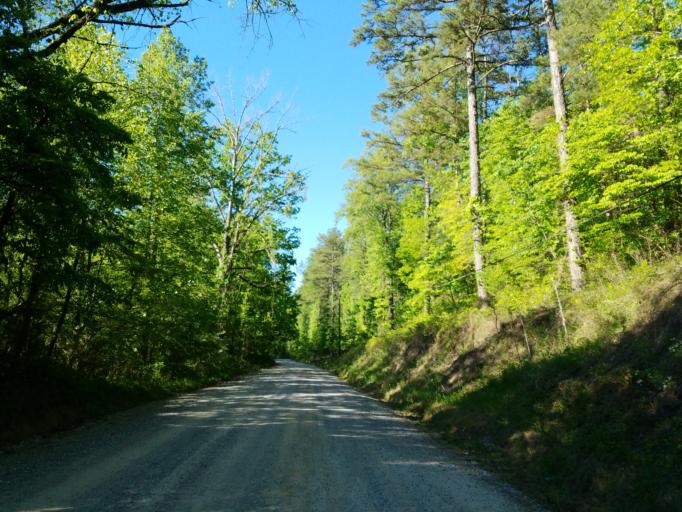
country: US
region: Georgia
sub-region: Gilmer County
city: Ellijay
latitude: 34.6303
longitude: -84.4997
